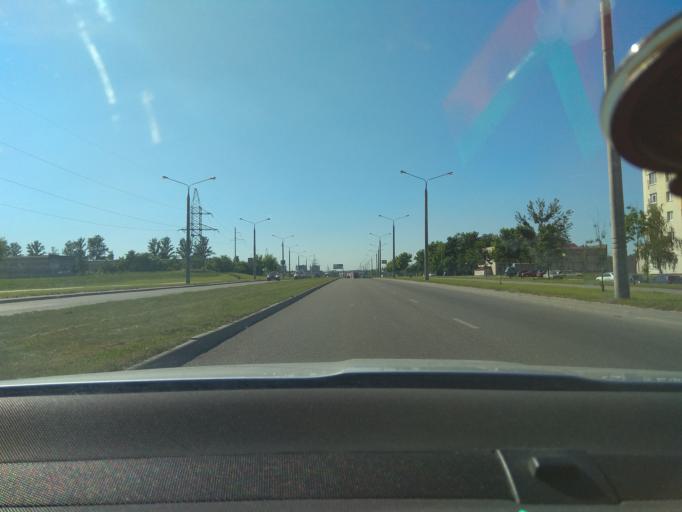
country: BY
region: Grodnenskaya
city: Hrodna
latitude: 53.6510
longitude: 23.7994
